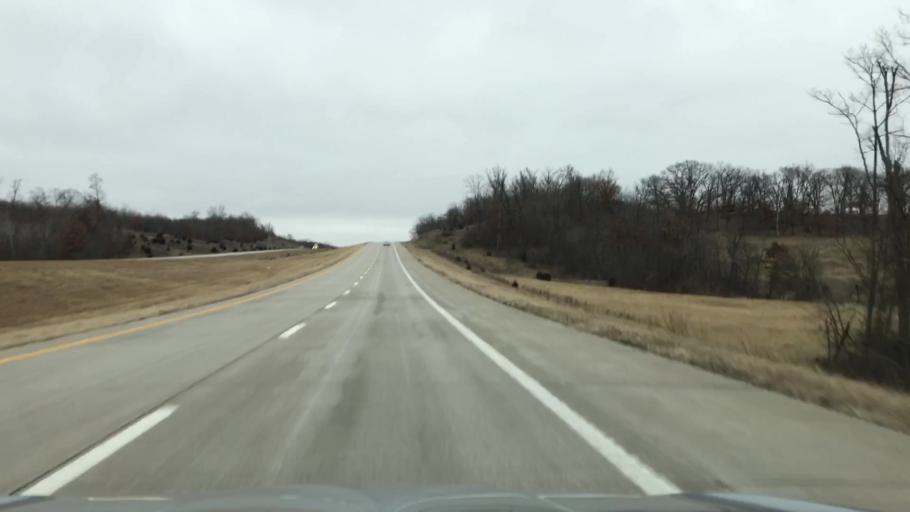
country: US
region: Missouri
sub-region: Linn County
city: Marceline
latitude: 39.7584
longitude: -92.8533
